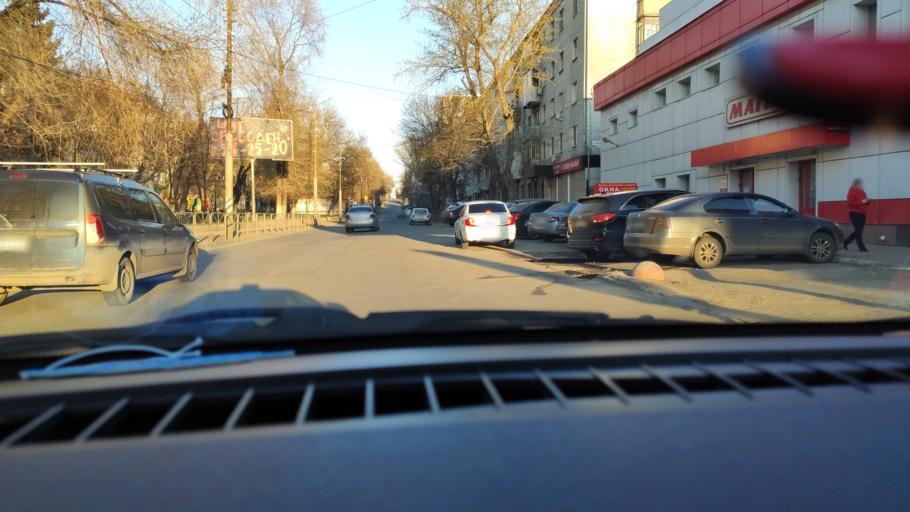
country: RU
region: Saratov
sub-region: Saratovskiy Rayon
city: Saratov
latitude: 51.5387
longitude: 46.0462
